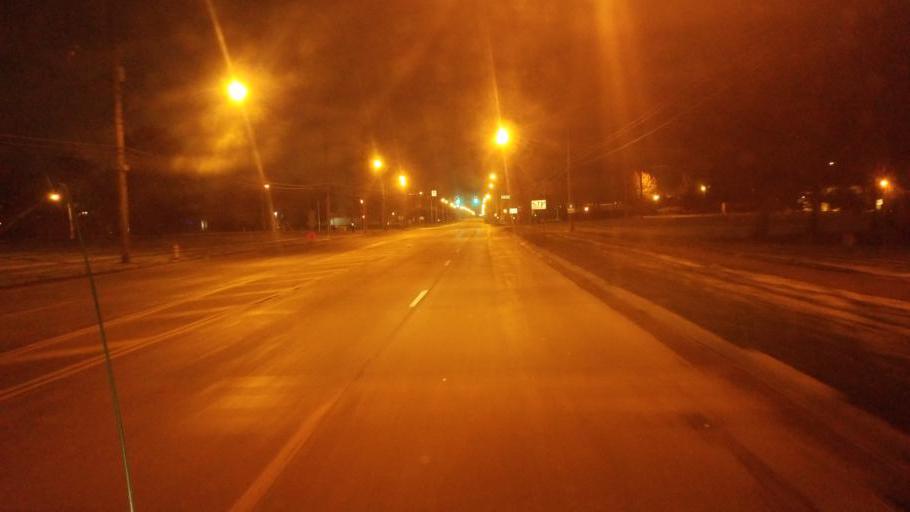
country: US
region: Ohio
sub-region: Cuyahoga County
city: Solon
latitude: 41.3860
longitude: -81.4690
